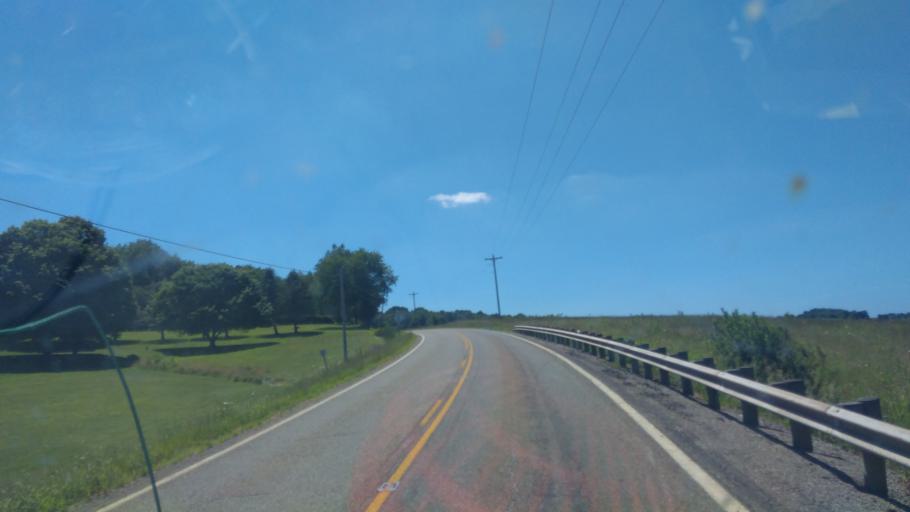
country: US
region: Ohio
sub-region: Columbiana County
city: Salineville
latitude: 40.6258
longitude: -80.8870
